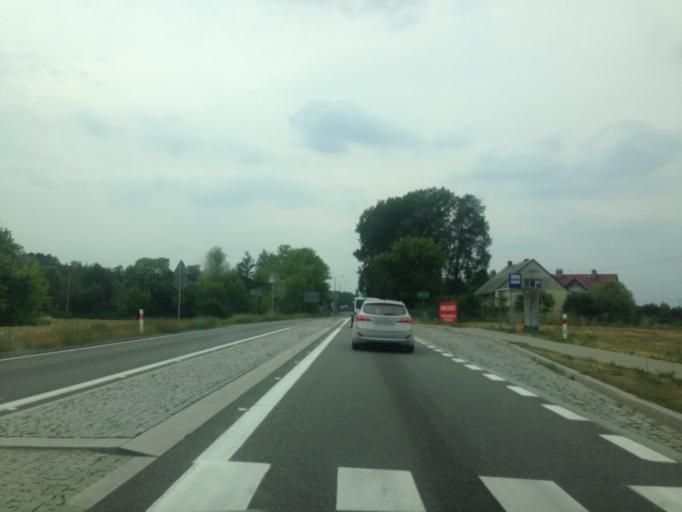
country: PL
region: Kujawsko-Pomorskie
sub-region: Powiat grudziadzki
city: Rogozno
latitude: 53.5024
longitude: 18.8648
